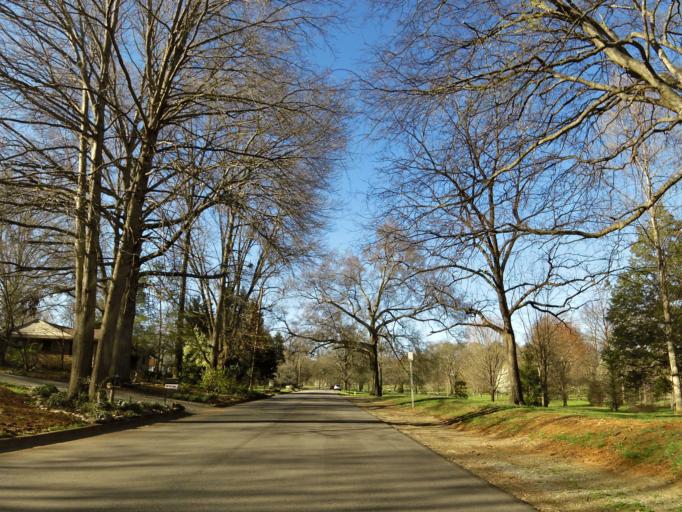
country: US
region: Tennessee
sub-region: Blount County
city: Alcoa
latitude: 35.7945
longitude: -83.9796
